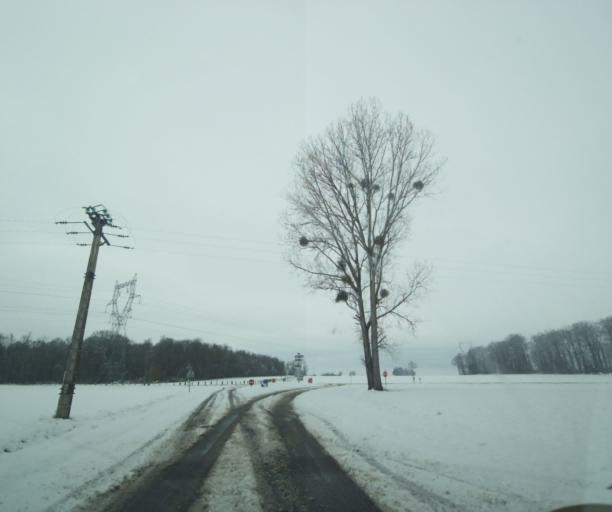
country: FR
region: Champagne-Ardenne
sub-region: Departement de la Haute-Marne
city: Montier-en-Der
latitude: 48.5085
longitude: 4.7489
